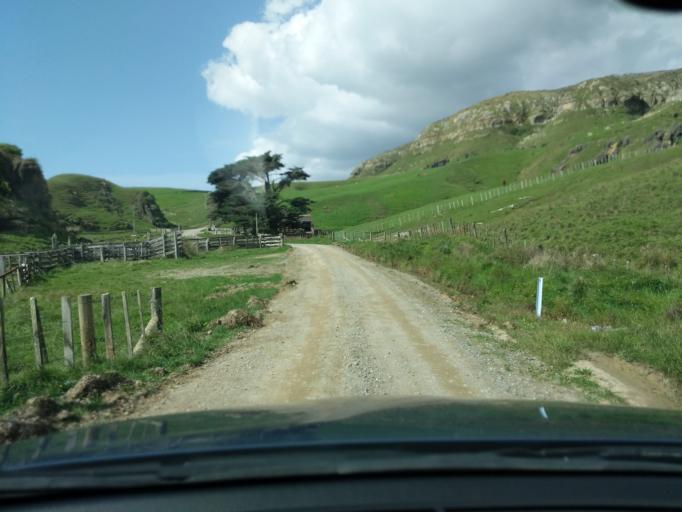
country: NZ
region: Tasman
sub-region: Tasman District
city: Takaka
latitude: -40.6513
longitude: 172.4227
